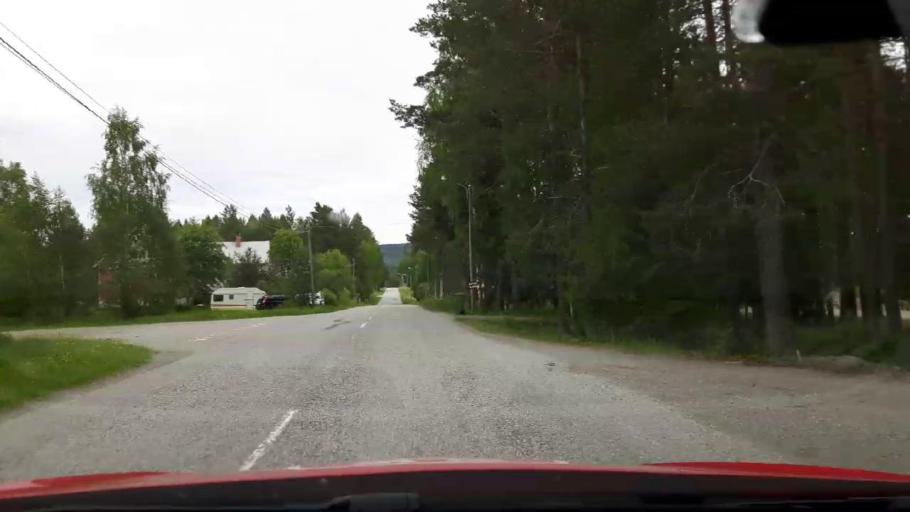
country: SE
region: Jaemtland
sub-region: Ragunda Kommun
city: Hammarstrand
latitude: 63.2185
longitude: 15.9396
